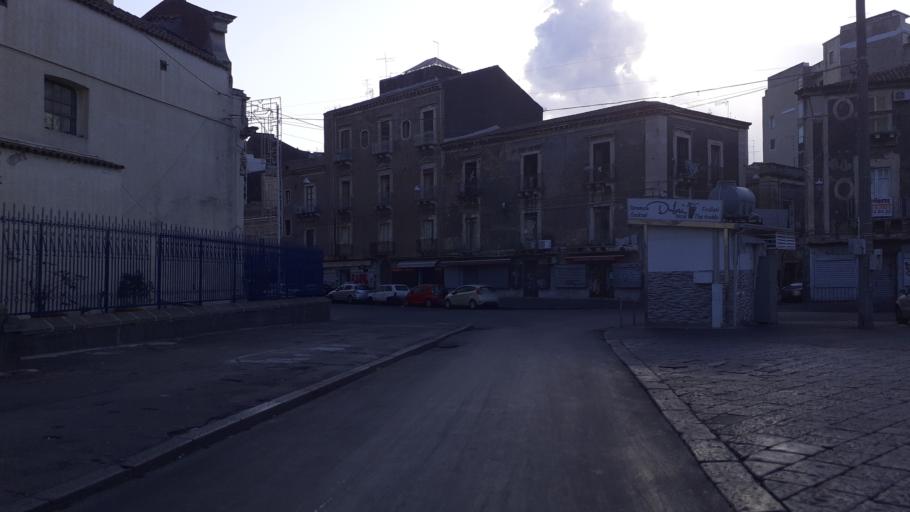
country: IT
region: Sicily
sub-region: Catania
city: Catania
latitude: 37.5089
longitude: 15.0884
